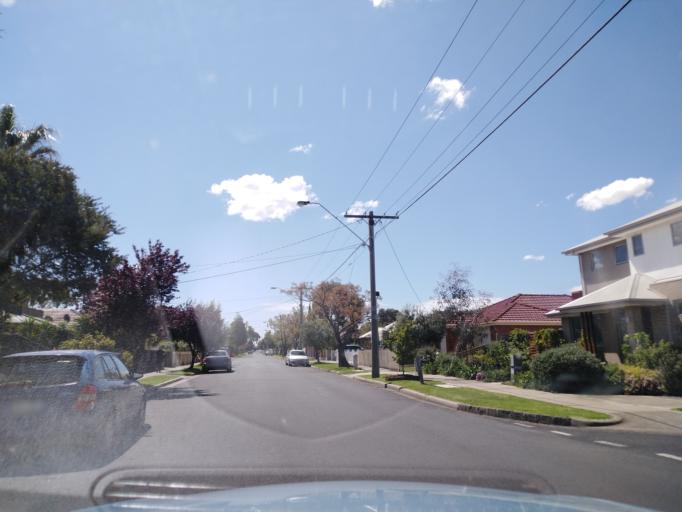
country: AU
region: Victoria
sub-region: Hobsons Bay
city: South Kingsville
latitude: -37.8386
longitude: 144.8647
